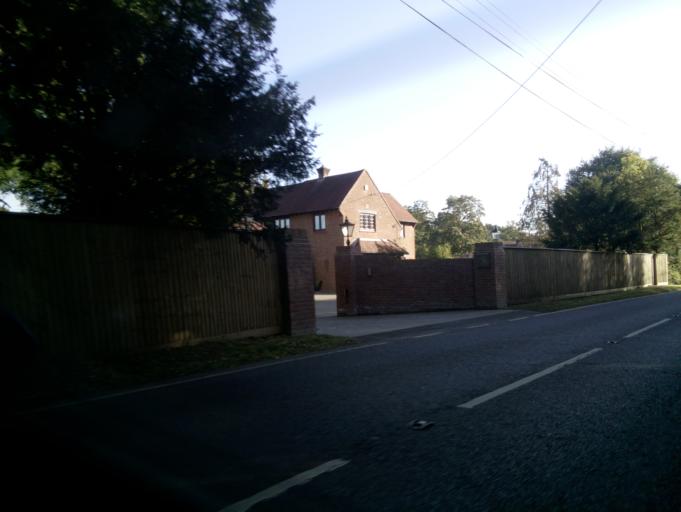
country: GB
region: England
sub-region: Hampshire
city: Bishops Waltham
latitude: 50.9297
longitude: -1.2403
